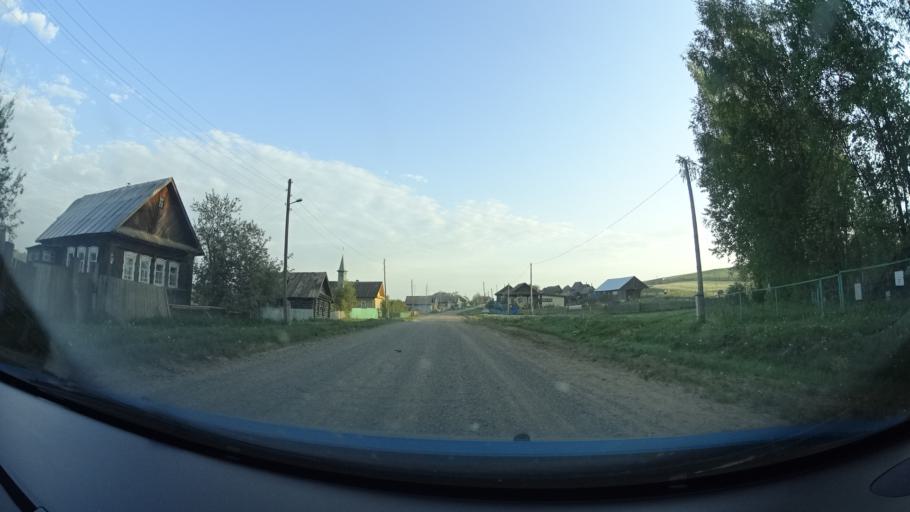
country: RU
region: Perm
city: Barda
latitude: 56.6818
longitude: 55.6906
